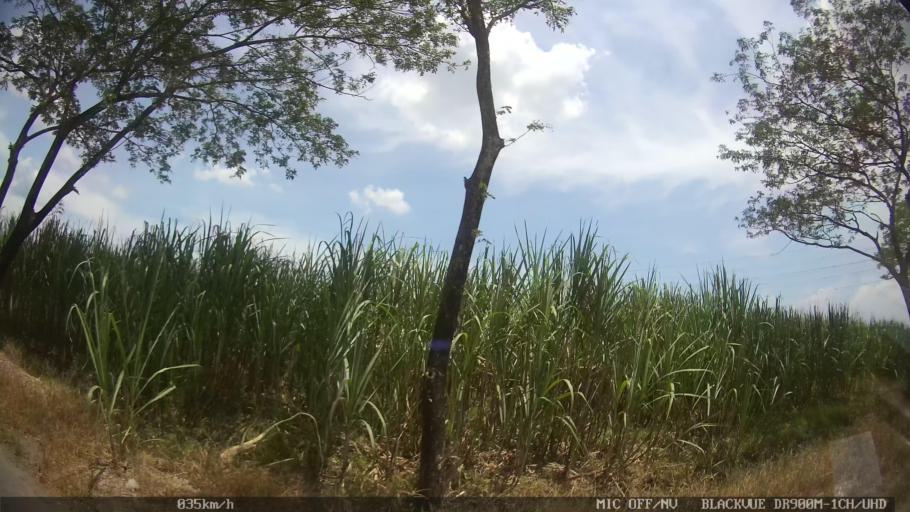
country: ID
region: North Sumatra
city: Binjai
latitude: 3.5913
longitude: 98.5297
